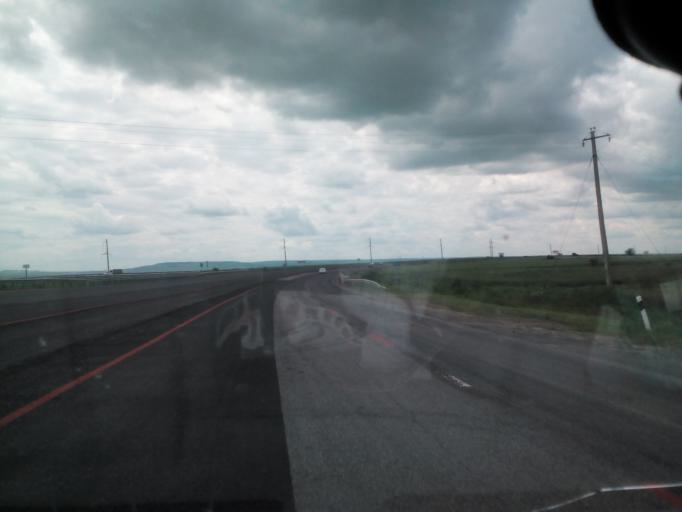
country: RU
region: Stavropol'skiy
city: Tatarka
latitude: 44.9565
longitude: 41.9893
